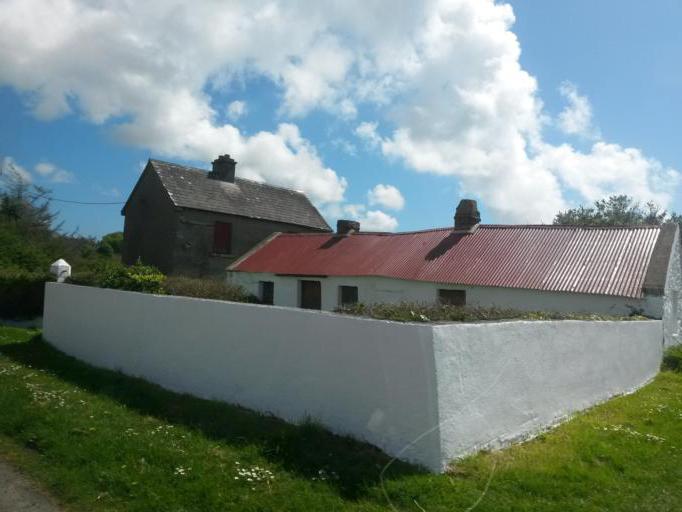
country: IE
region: Munster
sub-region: Waterford
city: Dunmore East
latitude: 52.2195
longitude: -6.9212
